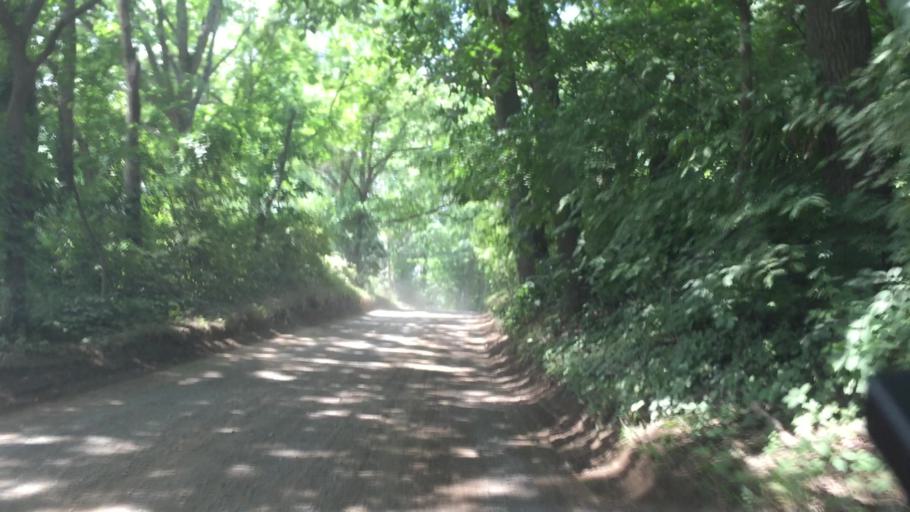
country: US
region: Michigan
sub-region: Oakland County
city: Auburn Hills
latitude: 42.6546
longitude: -83.2149
